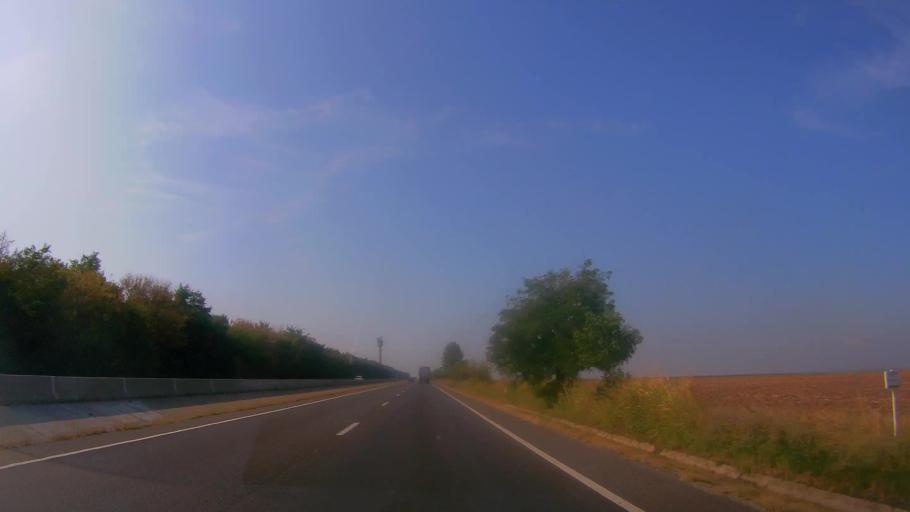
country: RO
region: Giurgiu
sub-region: Comuna Adunatii-Copaceni
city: Adunatii-Copaceni
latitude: 44.2323
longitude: 26.0334
